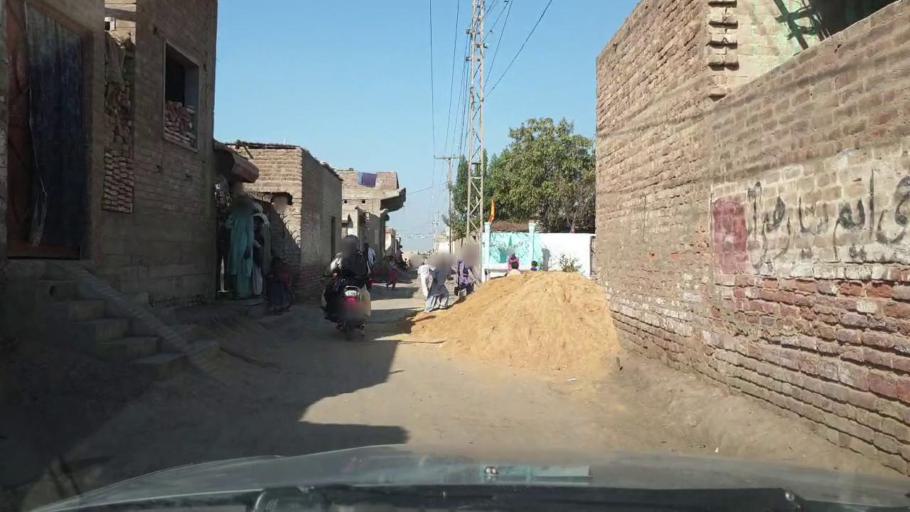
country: PK
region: Sindh
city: Tando Muhammad Khan
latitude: 25.1344
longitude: 68.5474
